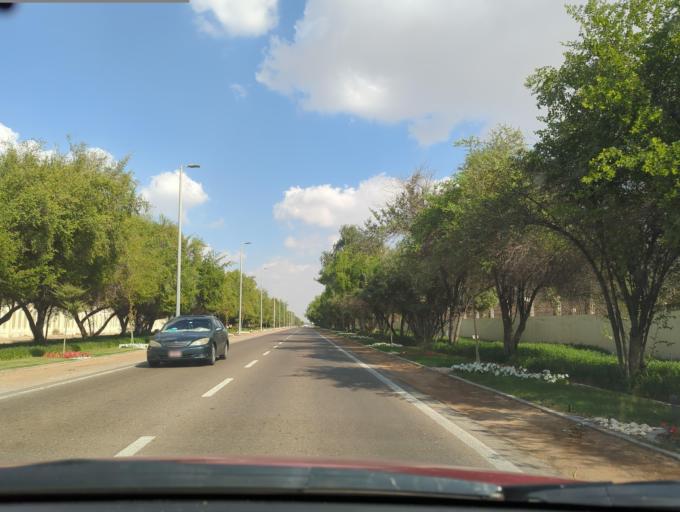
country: AE
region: Abu Dhabi
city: Al Ain
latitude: 24.1699
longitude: 55.6556
